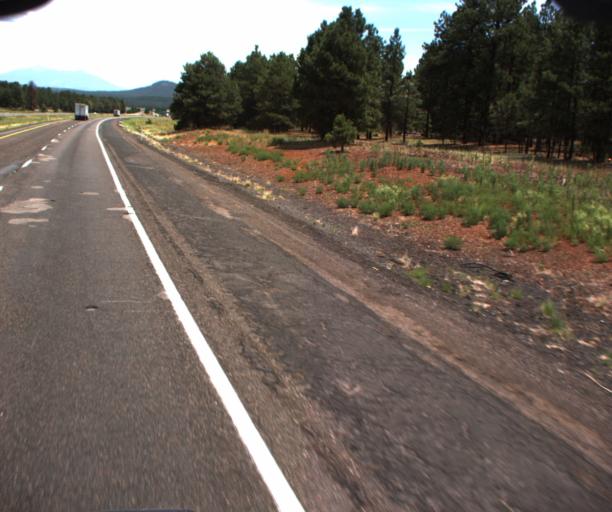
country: US
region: Arizona
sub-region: Coconino County
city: Parks
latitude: 35.2642
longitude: -112.0621
